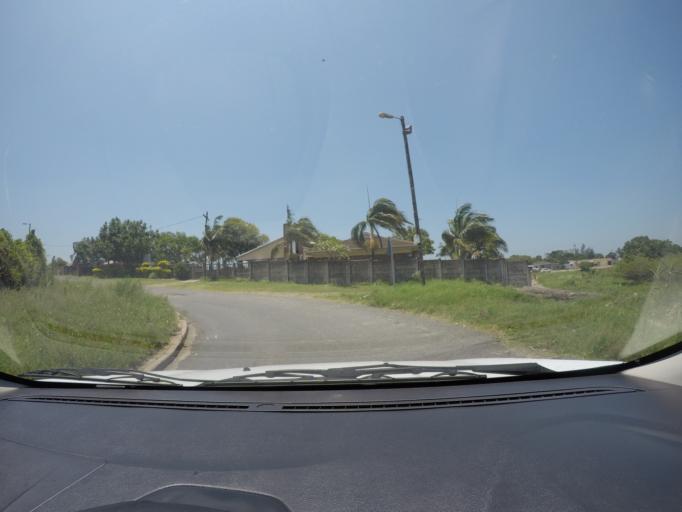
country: ZA
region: KwaZulu-Natal
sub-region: uThungulu District Municipality
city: eSikhawini
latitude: -28.8801
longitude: 31.9062
